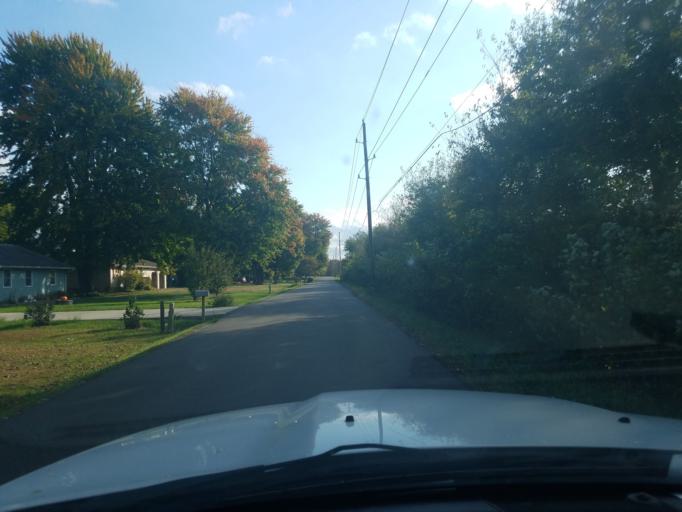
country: US
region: Indiana
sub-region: Jackson County
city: Seymour
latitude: 38.9655
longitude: -85.8479
